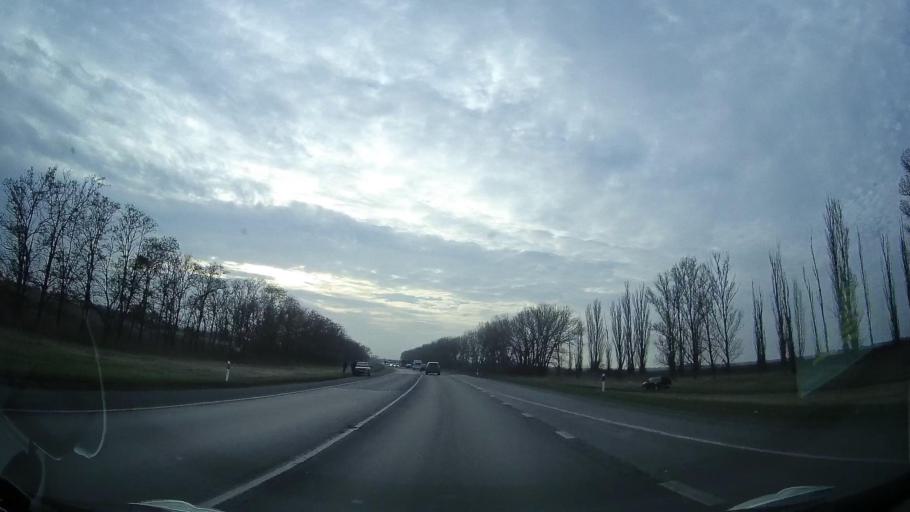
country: RU
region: Rostov
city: Starocherkasskaya
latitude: 47.1547
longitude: 40.1625
